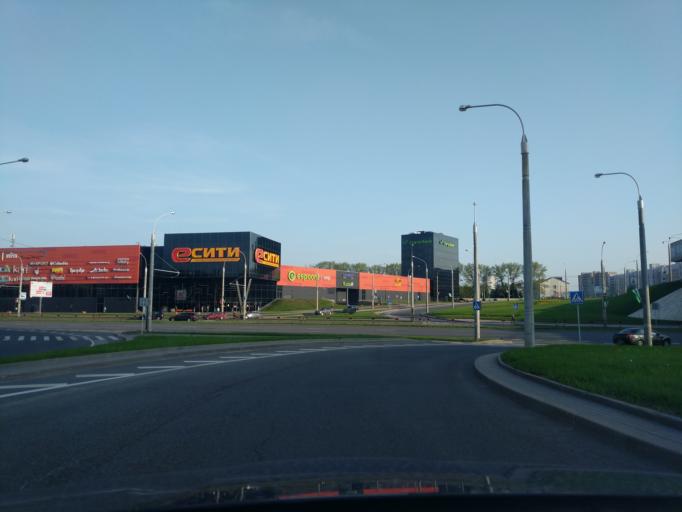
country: BY
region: Minsk
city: Minsk
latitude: 53.8731
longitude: 27.5707
